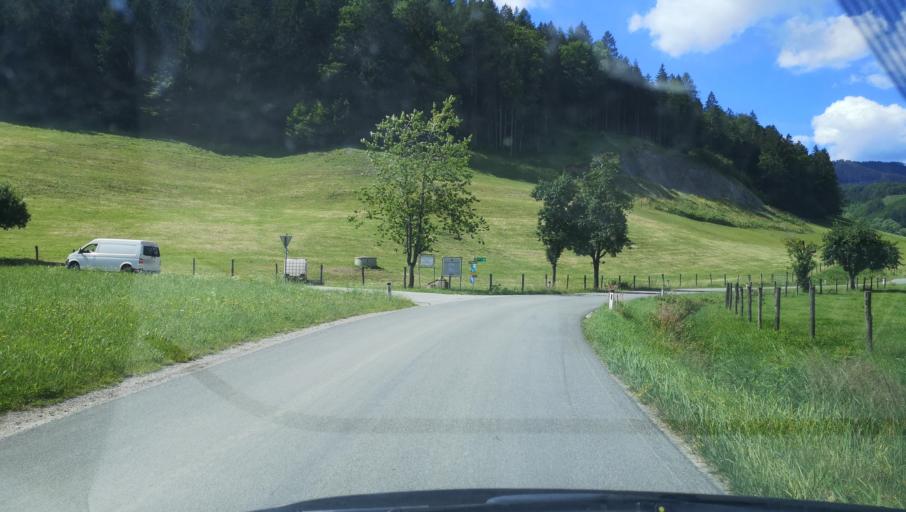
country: AT
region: Lower Austria
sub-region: Politischer Bezirk Scheibbs
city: Gresten
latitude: 47.9313
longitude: 15.0262
